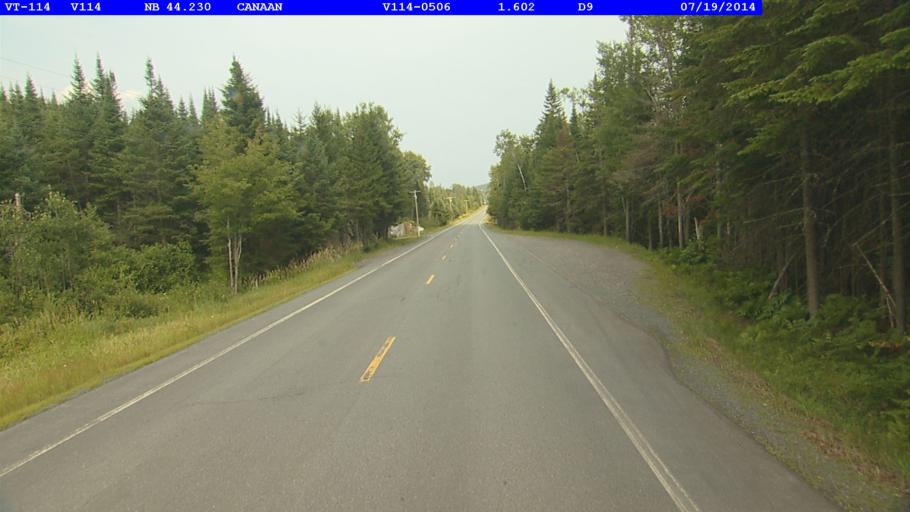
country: CA
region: Quebec
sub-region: Estrie
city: Coaticook
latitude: 45.0057
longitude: -71.6613
